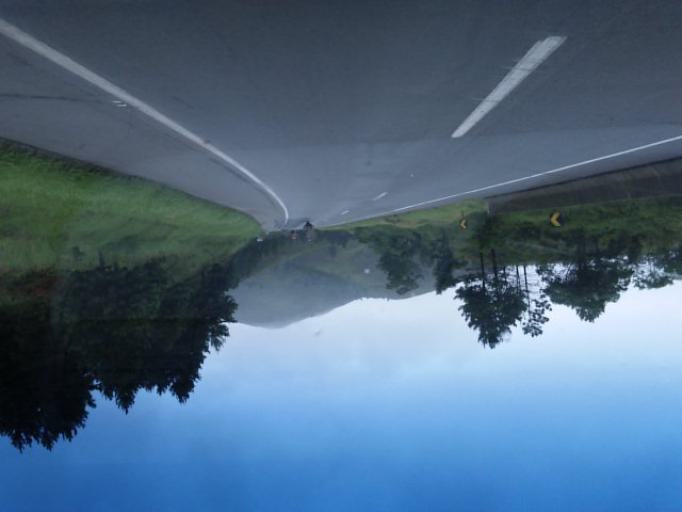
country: BR
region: Sao Paulo
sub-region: Cajati
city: Cajati
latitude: -24.9758
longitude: -48.5023
